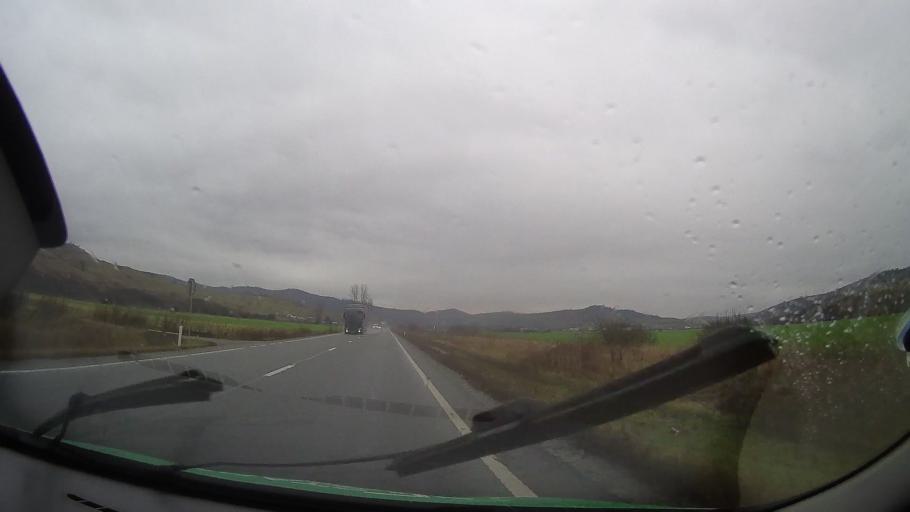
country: RO
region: Bistrita-Nasaud
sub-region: Comuna Teaca
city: Teaca
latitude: 46.9252
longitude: 24.4870
